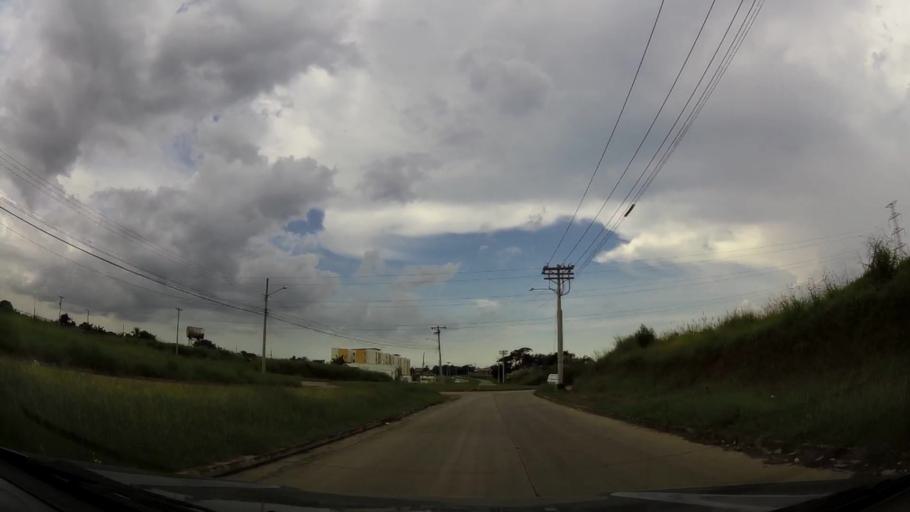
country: PA
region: Panama
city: Cabra Numero Uno
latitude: 9.1146
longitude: -79.3202
